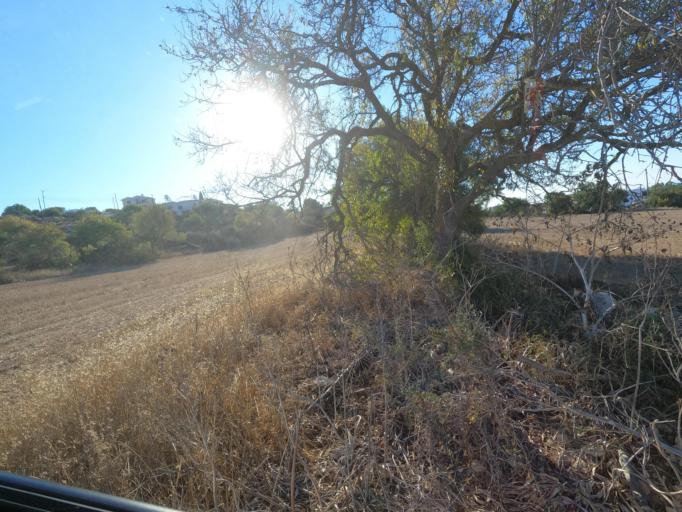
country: CY
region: Pafos
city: Mesogi
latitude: 34.7985
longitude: 32.4857
